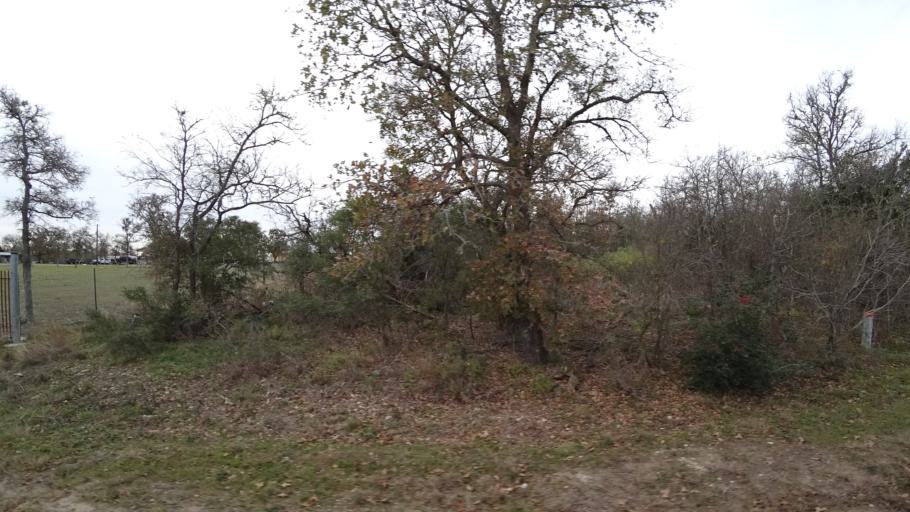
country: US
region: Texas
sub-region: Travis County
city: Garfield
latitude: 30.1072
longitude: -97.5704
